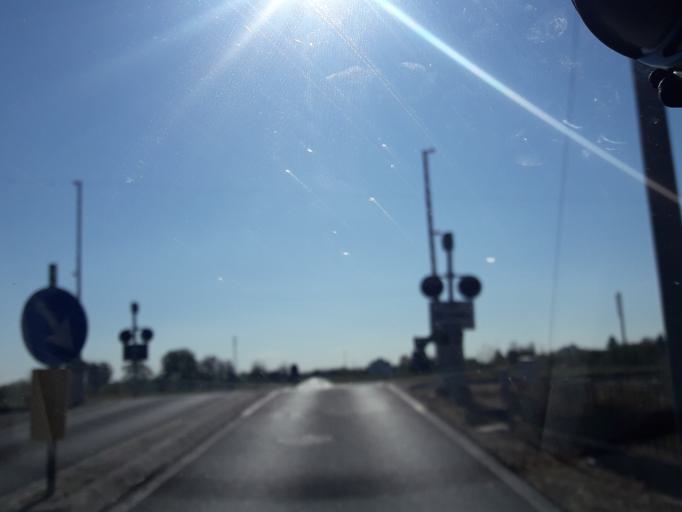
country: IT
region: Friuli Venezia Giulia
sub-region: Provincia di Udine
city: Udine
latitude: 46.0738
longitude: 13.2801
